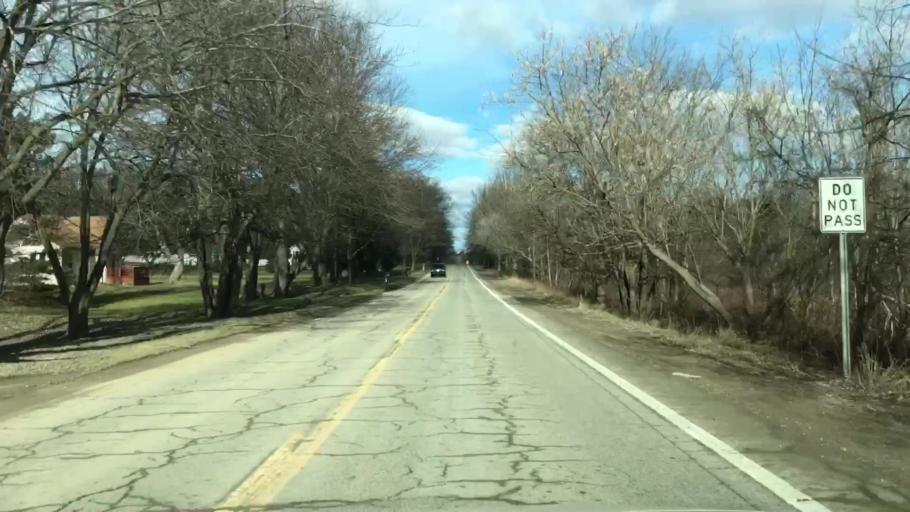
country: US
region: Michigan
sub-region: Oakland County
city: Lake Orion
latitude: 42.7623
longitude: -83.1978
